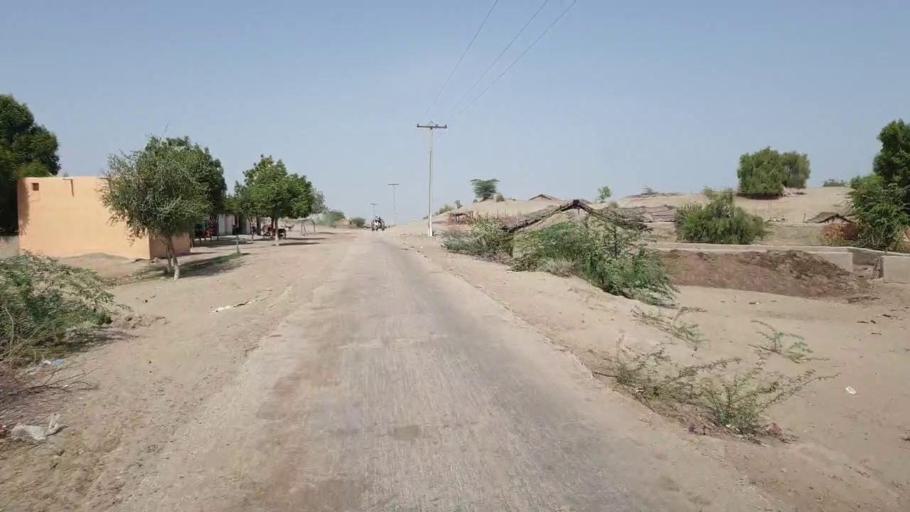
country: PK
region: Sindh
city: Jam Sahib
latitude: 26.4077
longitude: 68.8906
